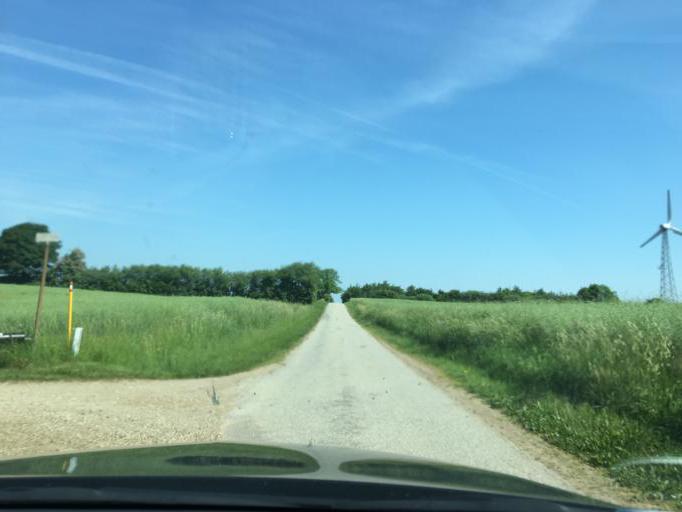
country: DK
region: South Denmark
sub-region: Kolding Kommune
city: Kolding
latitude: 55.5501
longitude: 9.4700
